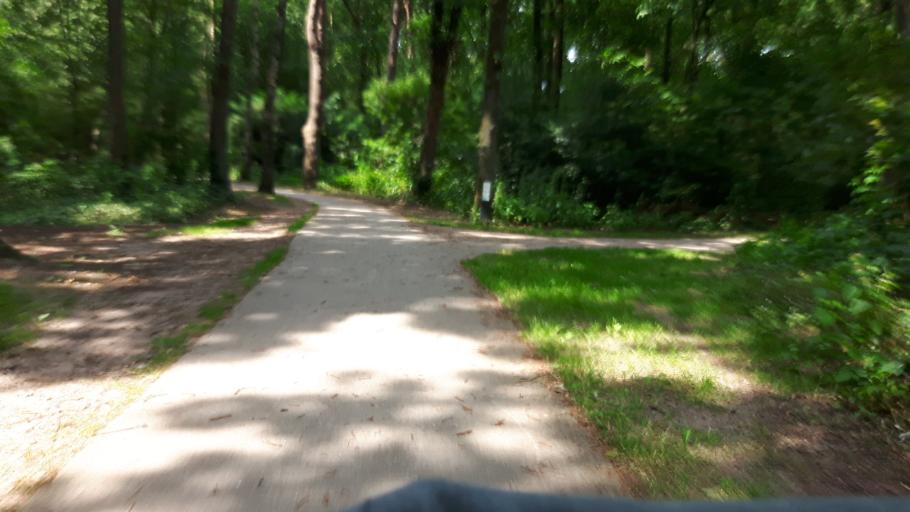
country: NL
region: Utrecht
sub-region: Gemeente Soest
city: Soest
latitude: 52.1565
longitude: 5.2979
